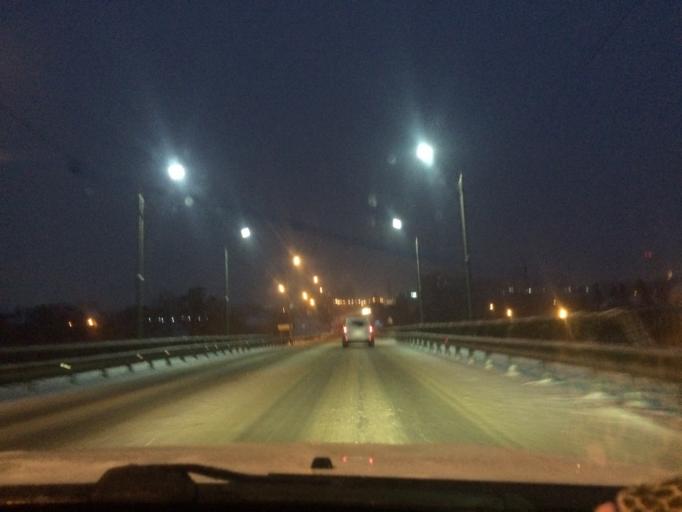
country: RU
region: Tula
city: Mendeleyevskiy
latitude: 54.1576
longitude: 37.5629
